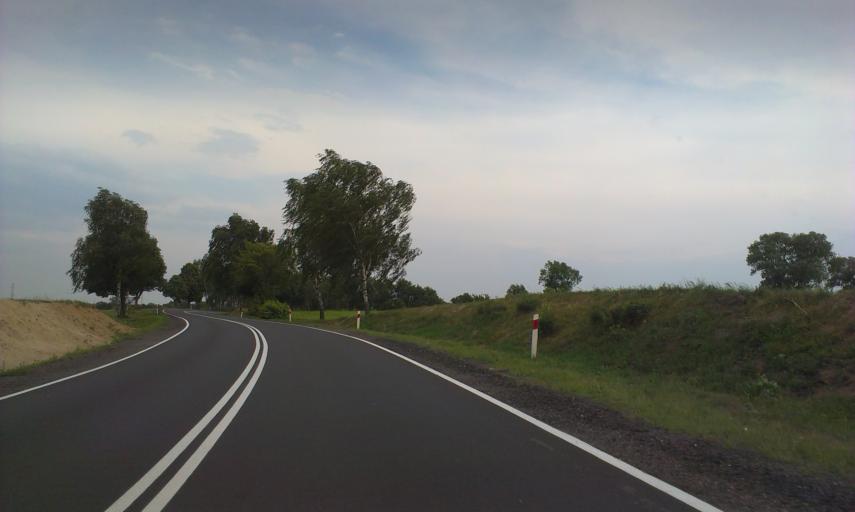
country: PL
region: West Pomeranian Voivodeship
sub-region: Powiat szczecinecki
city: Szczecinek
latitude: 53.7583
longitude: 16.6484
